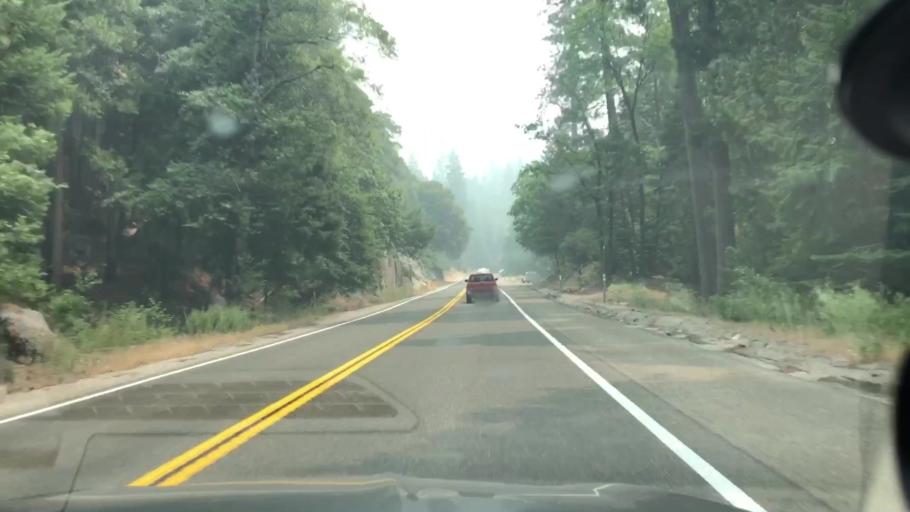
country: US
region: California
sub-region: El Dorado County
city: Pollock Pines
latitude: 38.7771
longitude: -120.2780
